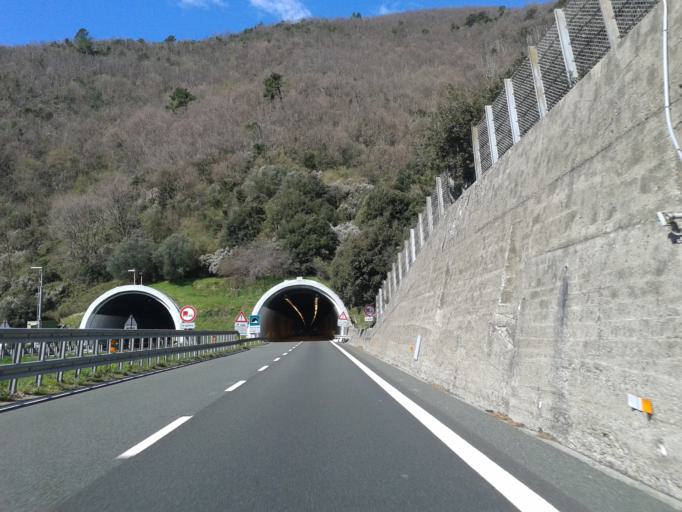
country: IT
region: Liguria
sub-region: Provincia di La Spezia
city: Deiva Marina
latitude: 44.2457
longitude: 9.5392
